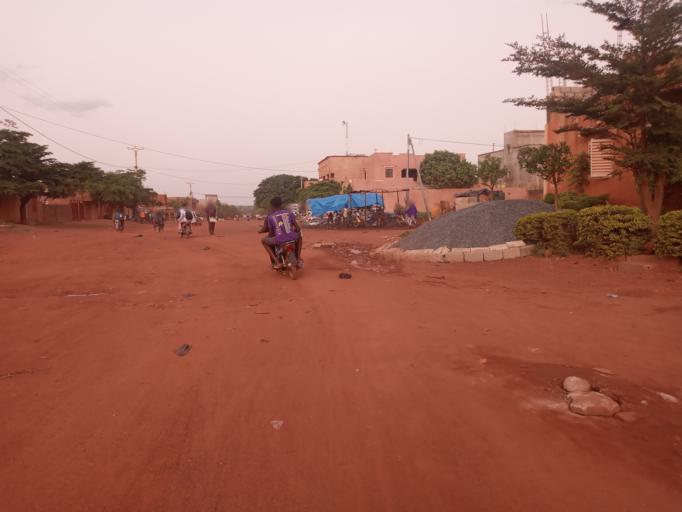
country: ML
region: Bamako
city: Bamako
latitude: 12.5579
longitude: -7.9853
